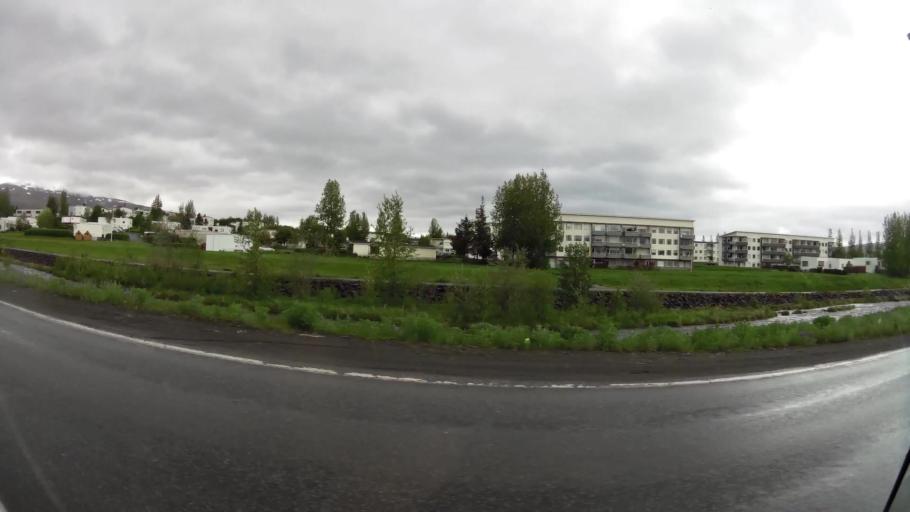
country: IS
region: Northeast
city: Akureyri
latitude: 65.6878
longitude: -18.1062
